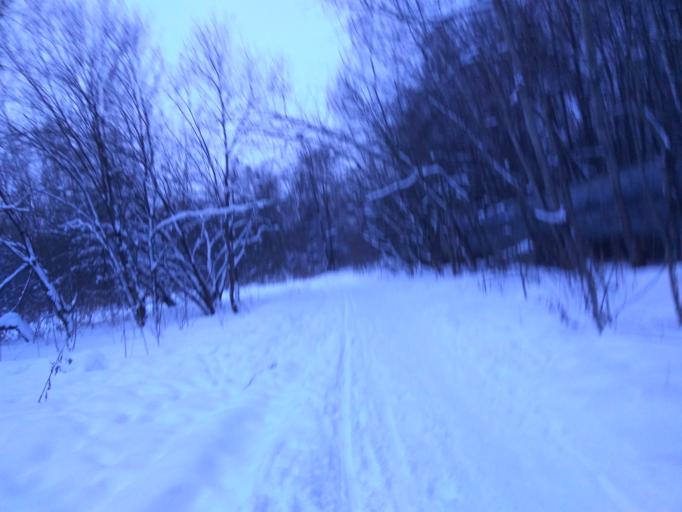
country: RU
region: Moscow
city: Biryulevo
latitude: 55.5903
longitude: 37.6996
